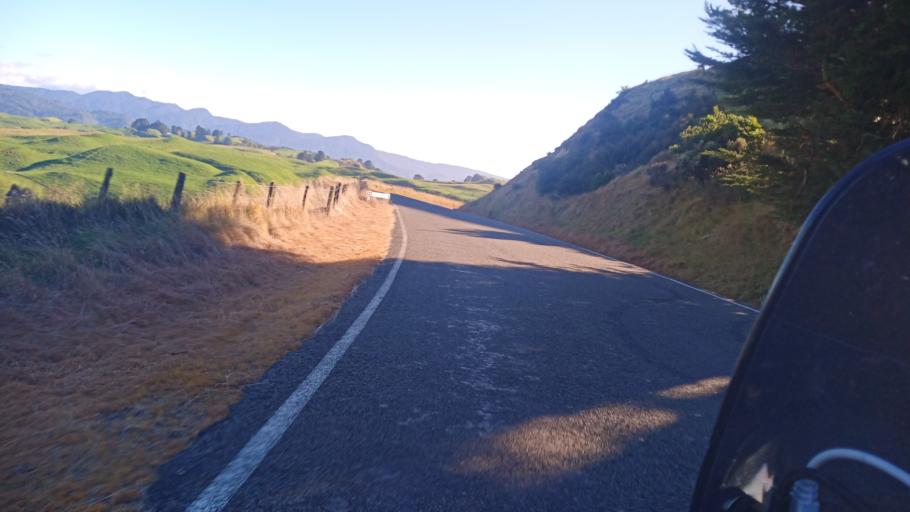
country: NZ
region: Hawke's Bay
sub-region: Wairoa District
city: Wairoa
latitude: -38.8466
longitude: 177.2540
